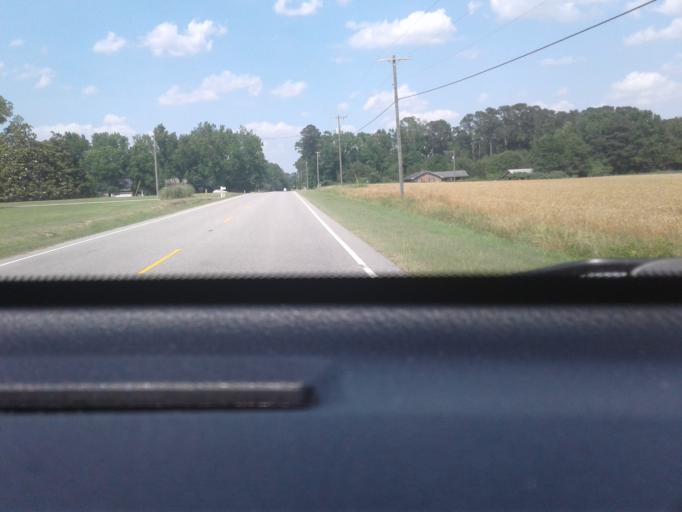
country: US
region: North Carolina
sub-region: Cumberland County
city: Eastover
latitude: 35.1304
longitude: -78.7542
